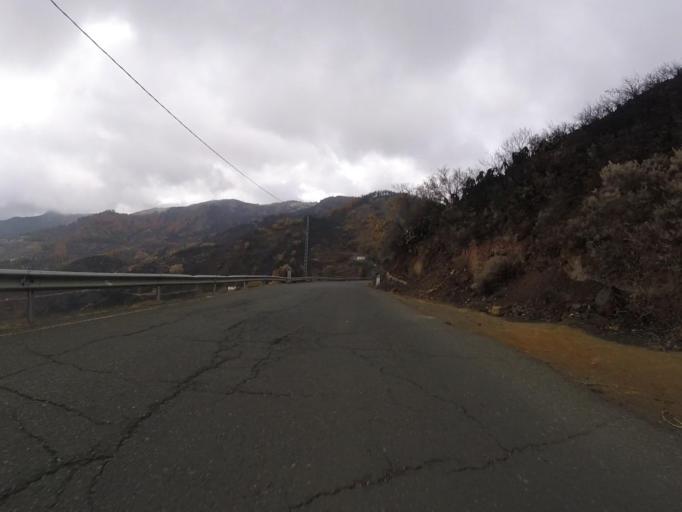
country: ES
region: Canary Islands
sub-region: Provincia de Las Palmas
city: Tejeda
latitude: 27.9874
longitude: -15.5758
